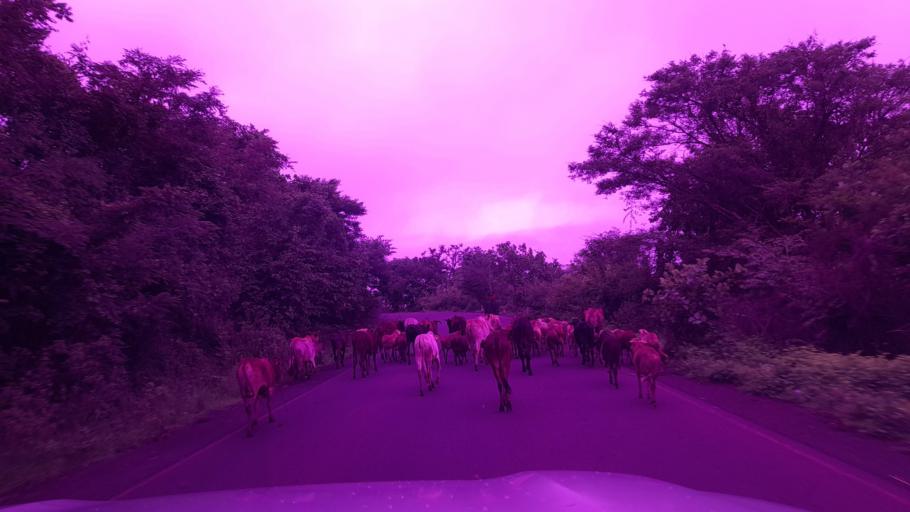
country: ET
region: Oromiya
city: Waliso
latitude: 8.1740
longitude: 37.5827
